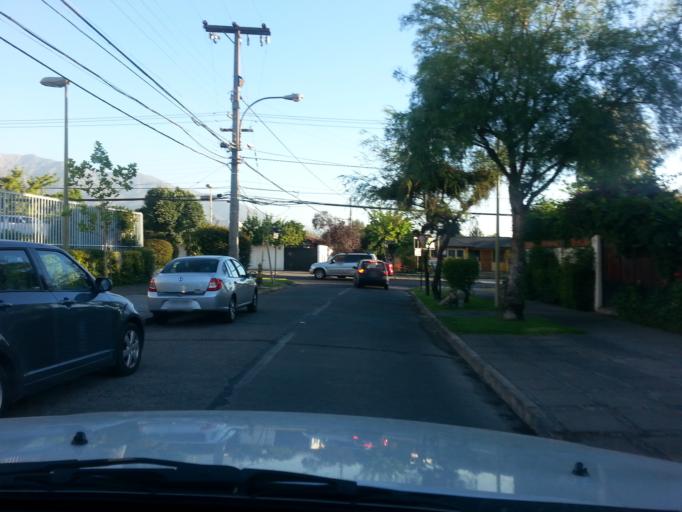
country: CL
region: Santiago Metropolitan
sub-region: Provincia de Santiago
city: Villa Presidente Frei, Nunoa, Santiago, Chile
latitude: -33.4252
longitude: -70.5661
